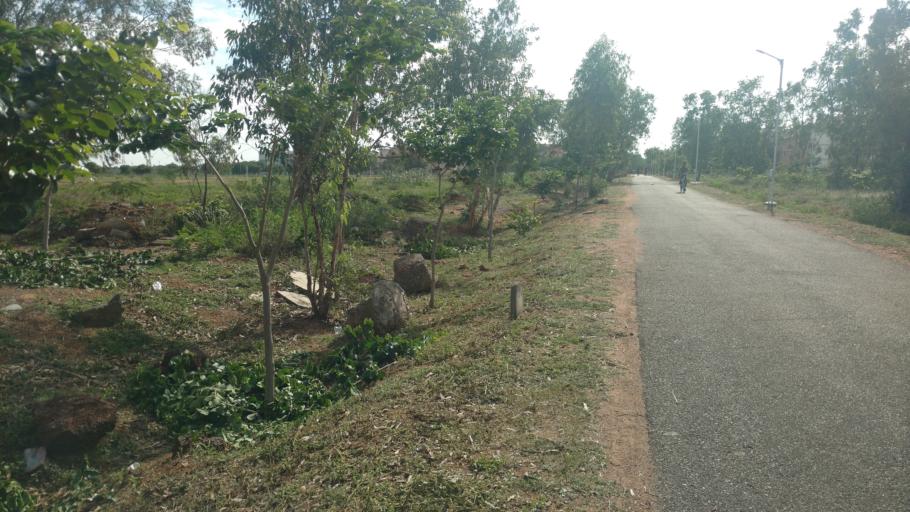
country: IN
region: Tamil Nadu
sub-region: Tiruchchirappalli
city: Lalgudi
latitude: 10.7671
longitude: 78.8146
